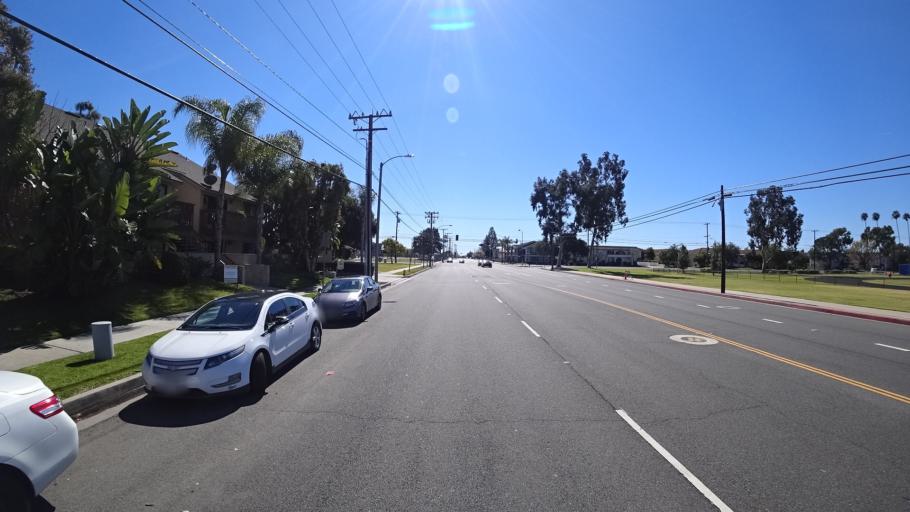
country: US
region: California
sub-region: Orange County
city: Cypress
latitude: 33.8254
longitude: -118.0196
